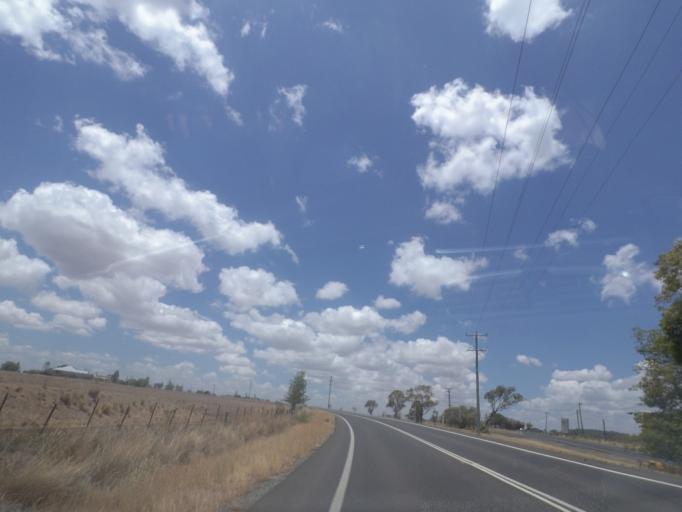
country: AU
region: Queensland
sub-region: Toowoomba
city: Top Camp
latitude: -27.7322
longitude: 151.9123
